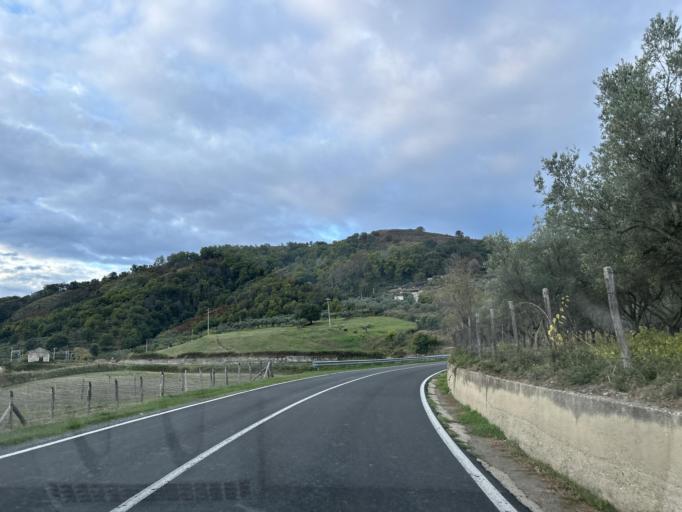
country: IT
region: Calabria
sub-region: Provincia di Catanzaro
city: Montauro
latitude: 38.7578
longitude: 16.5072
